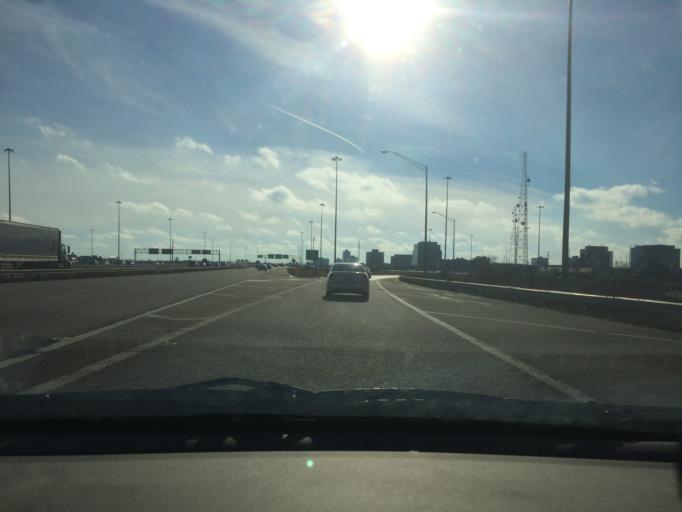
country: US
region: Illinois
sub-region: Cook County
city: Rolling Meadows
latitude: 42.0613
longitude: -88.0286
